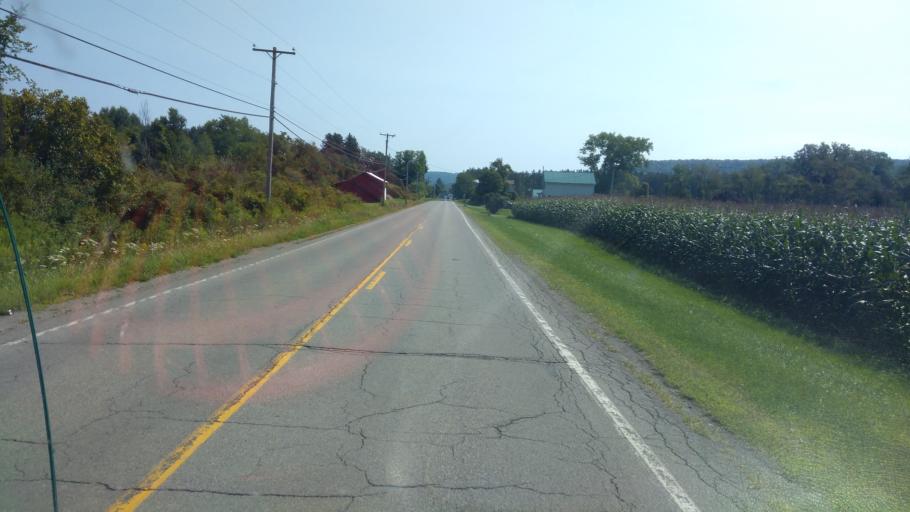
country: US
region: New York
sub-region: Allegany County
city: Friendship
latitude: 42.2011
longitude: -78.1582
